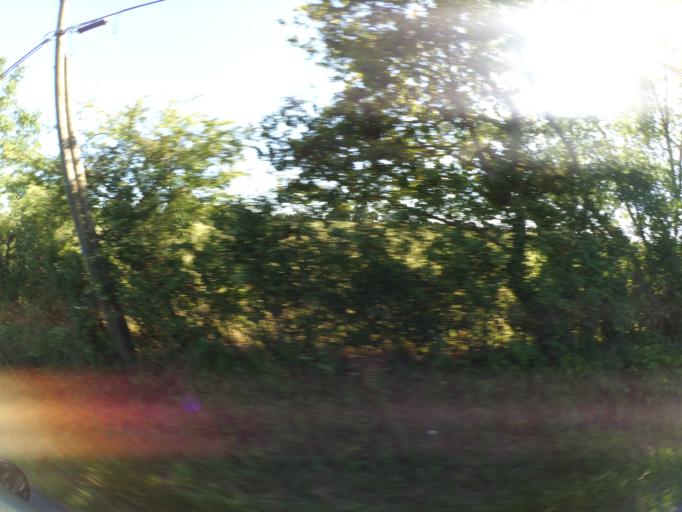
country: FR
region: Pays de la Loire
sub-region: Departement de la Vendee
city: Les Herbiers
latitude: 46.8914
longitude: -1.0494
